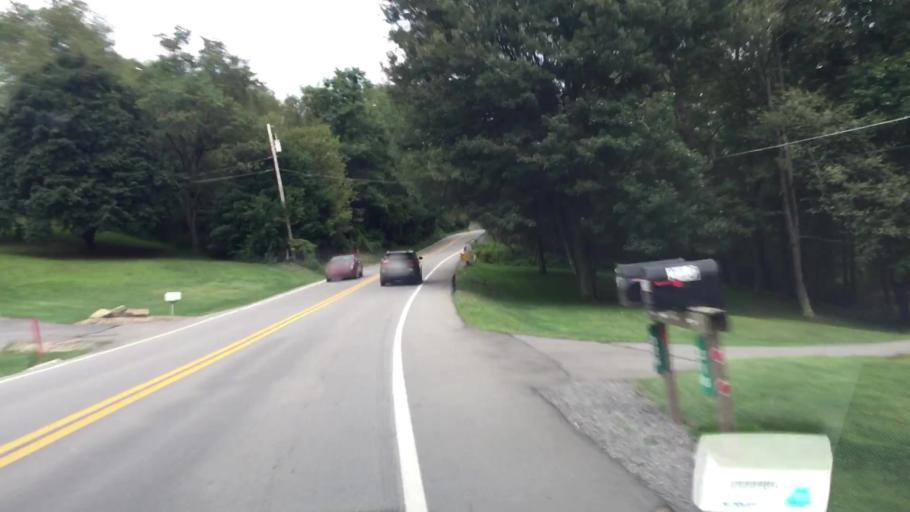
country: US
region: Pennsylvania
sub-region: Butler County
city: Evans City
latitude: 40.7655
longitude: -80.1001
